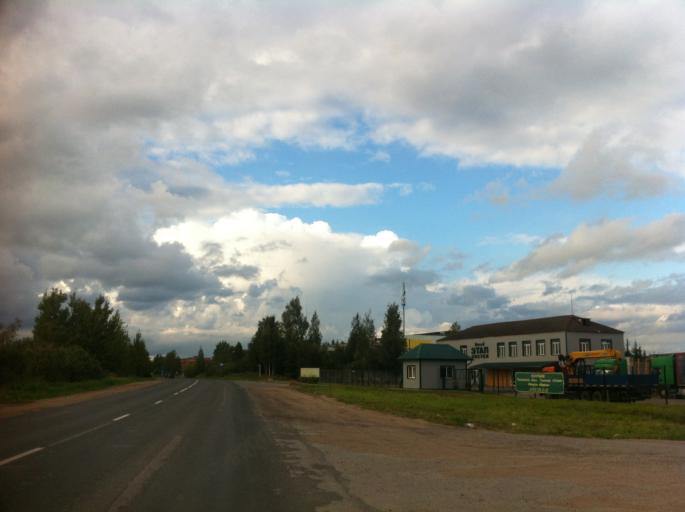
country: RU
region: Pskov
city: Pskov
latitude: 57.8492
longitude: 28.3076
